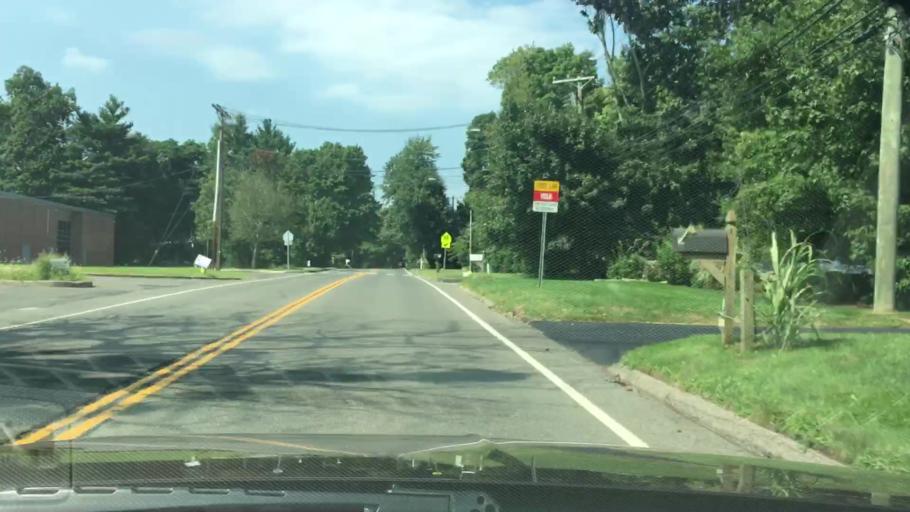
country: US
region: Connecticut
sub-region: Fairfield County
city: Norwalk
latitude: 41.1341
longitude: -73.4140
